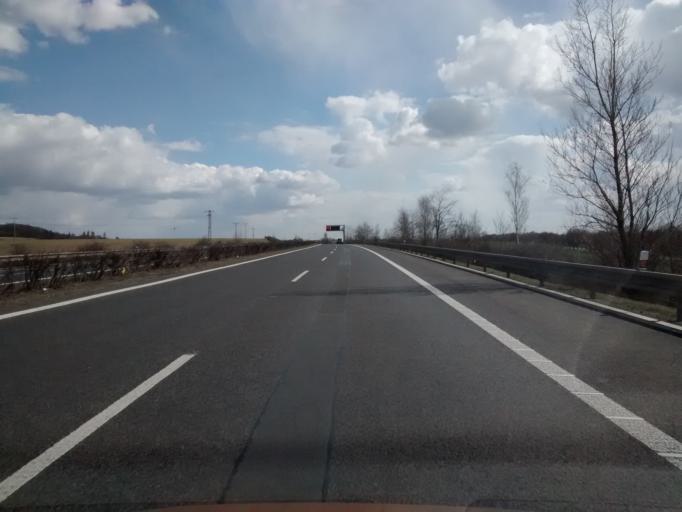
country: CZ
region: Central Bohemia
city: Velvary
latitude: 50.3349
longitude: 14.2856
